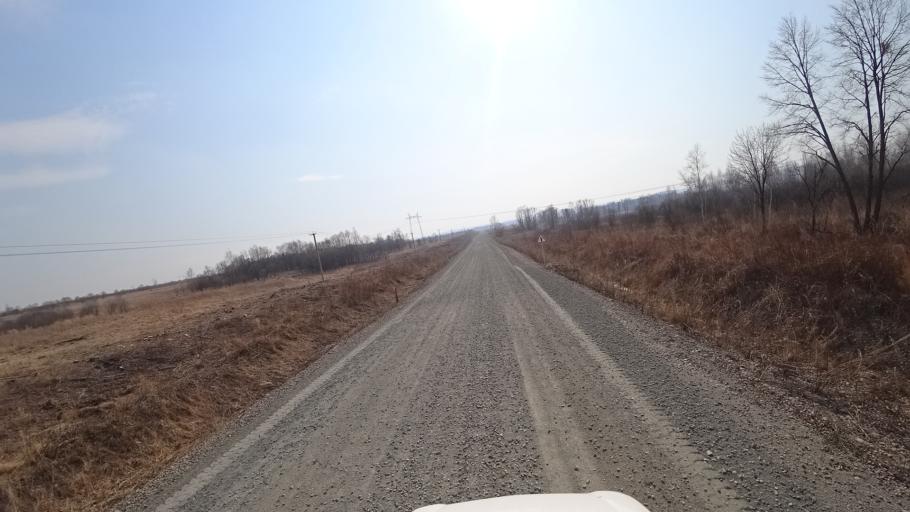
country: RU
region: Amur
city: Novobureyskiy
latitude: 49.8173
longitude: 129.9778
